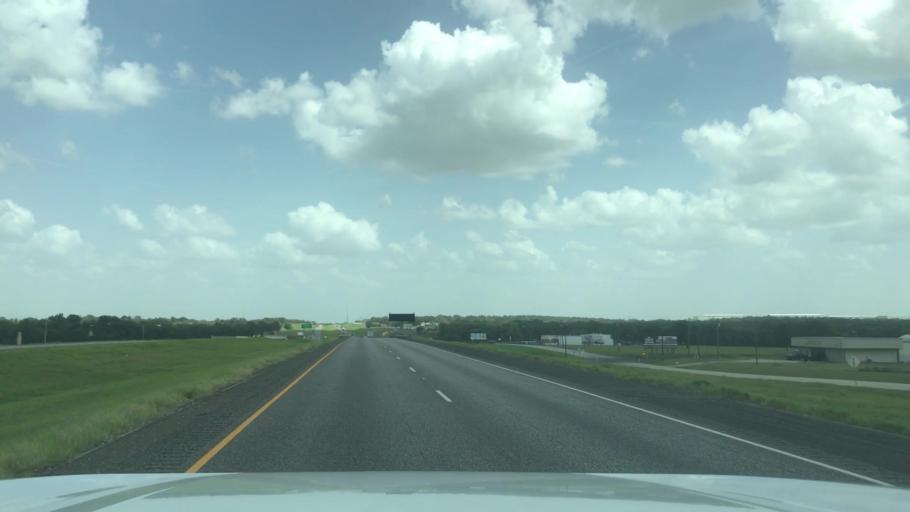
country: US
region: Texas
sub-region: Brazos County
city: Bryan
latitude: 30.7483
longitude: -96.4584
